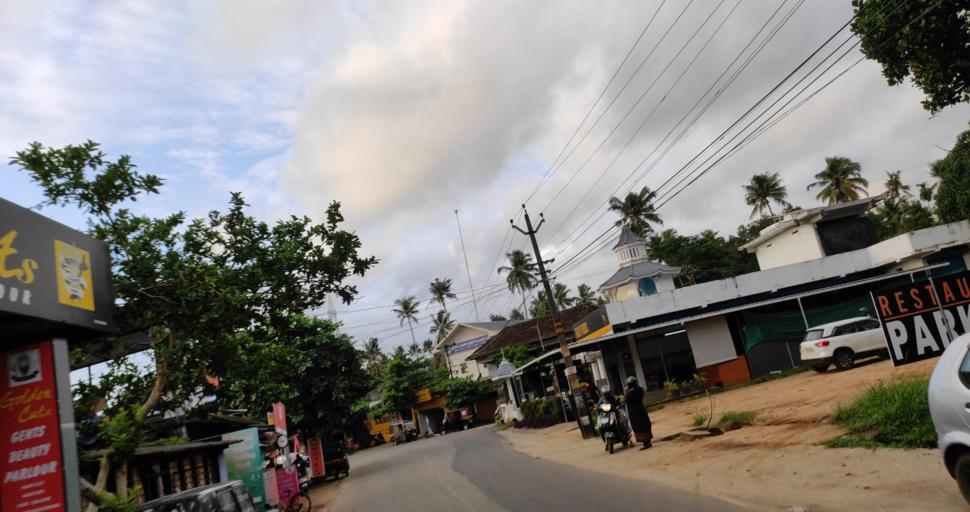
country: IN
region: Kerala
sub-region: Thrissur District
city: Kizhake Chalakudi
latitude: 10.3135
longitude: 76.3887
